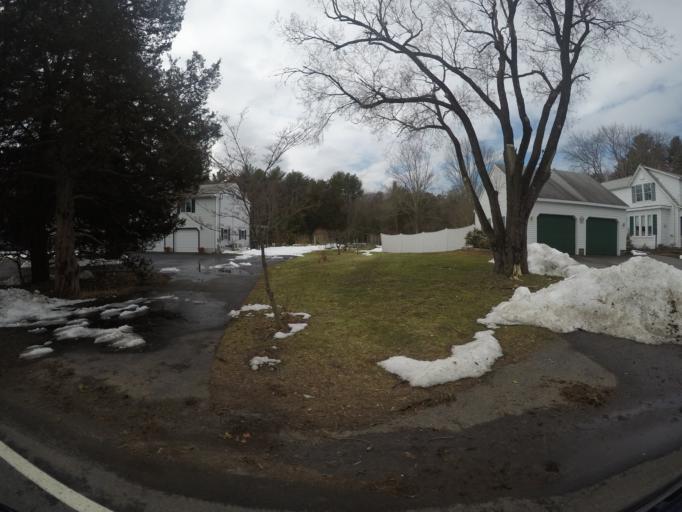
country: US
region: Massachusetts
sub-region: Bristol County
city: Easton
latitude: 42.0353
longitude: -71.1216
